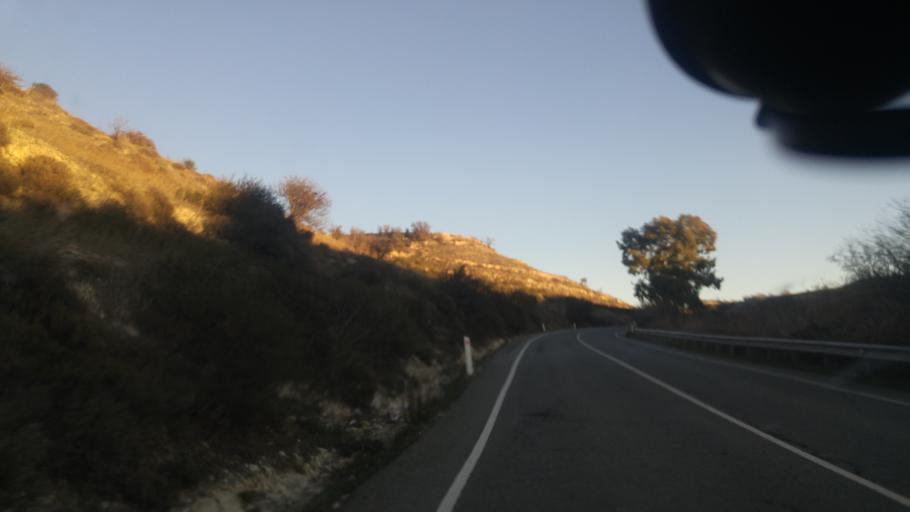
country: CY
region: Limassol
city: Pachna
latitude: 34.8010
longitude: 32.7954
